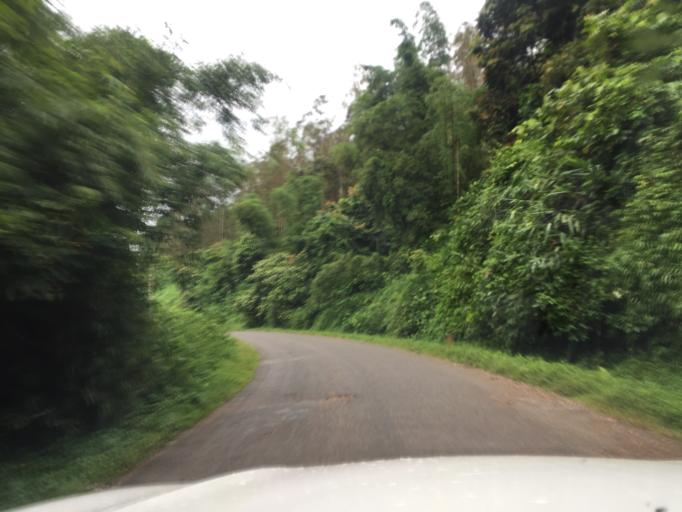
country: LA
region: Oudomxai
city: Muang La
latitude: 20.9905
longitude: 102.2280
